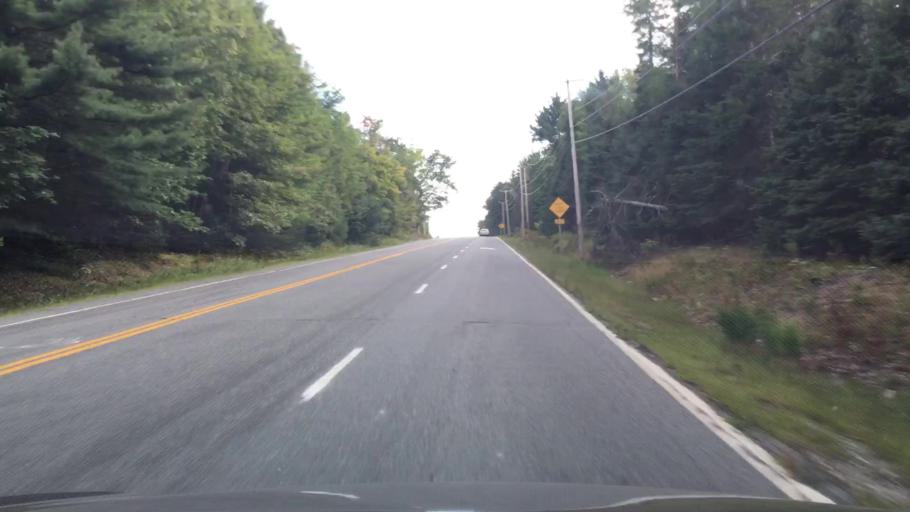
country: US
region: Maine
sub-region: Hancock County
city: Surry
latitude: 44.4912
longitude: -68.5090
